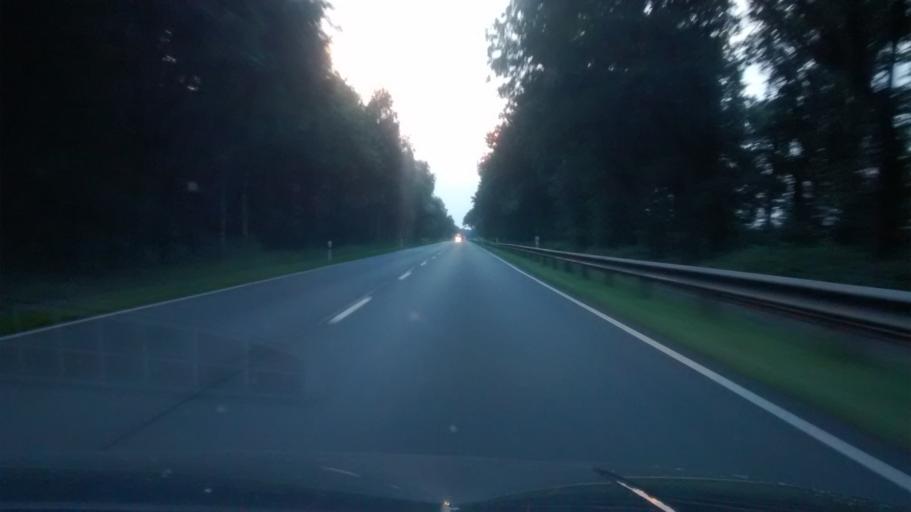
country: DE
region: Lower Saxony
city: Haselunne
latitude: 52.6874
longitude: 7.4462
